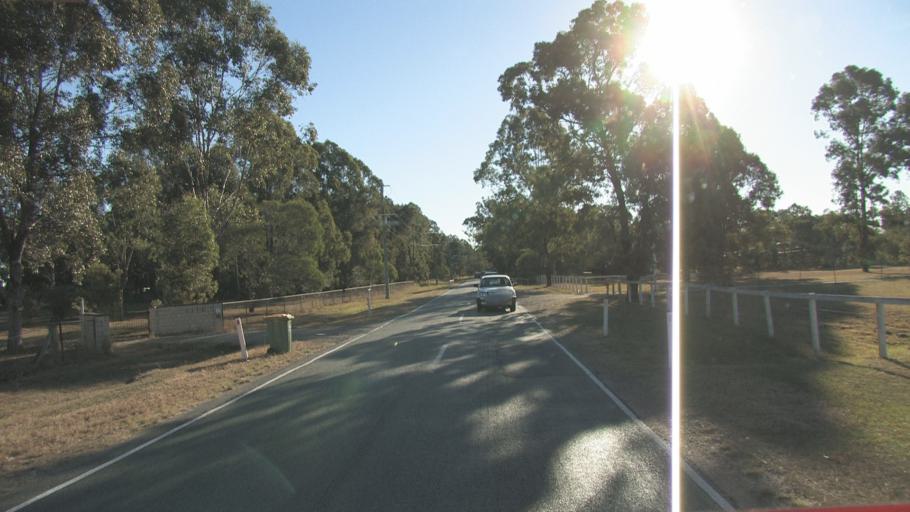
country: AU
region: Queensland
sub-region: Logan
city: Chambers Flat
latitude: -27.7543
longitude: 153.0840
